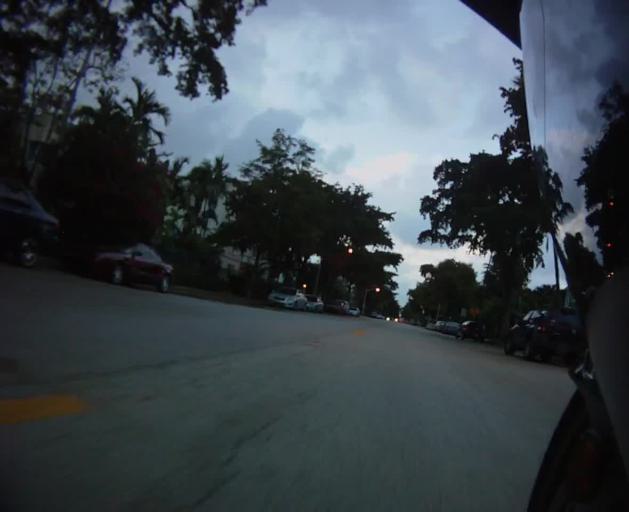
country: US
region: Florida
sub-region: Miami-Dade County
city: Miami Beach
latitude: 25.7761
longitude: -80.1383
